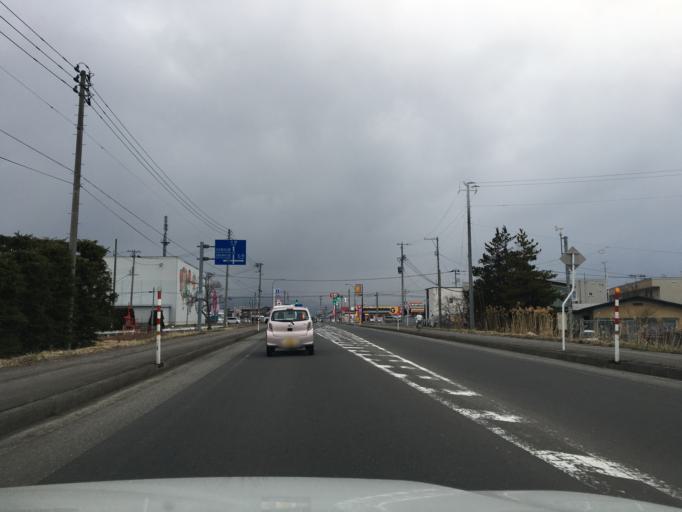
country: JP
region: Aomori
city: Kuroishi
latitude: 40.5875
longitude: 140.5689
